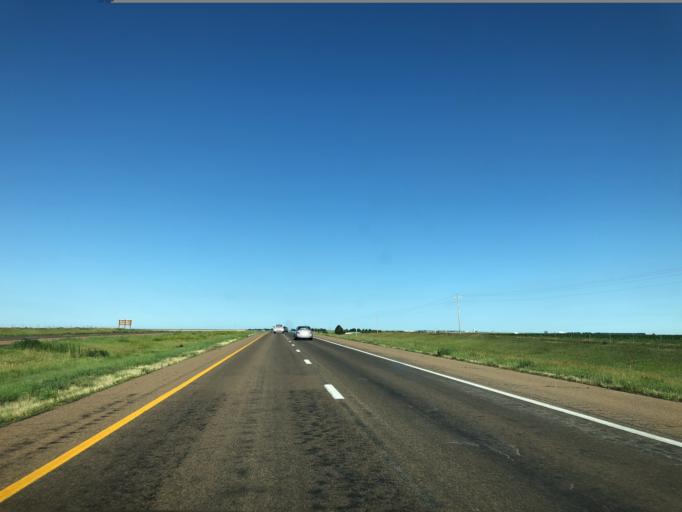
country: US
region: Kansas
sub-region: Thomas County
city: Colby
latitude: 39.3653
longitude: -101.1209
